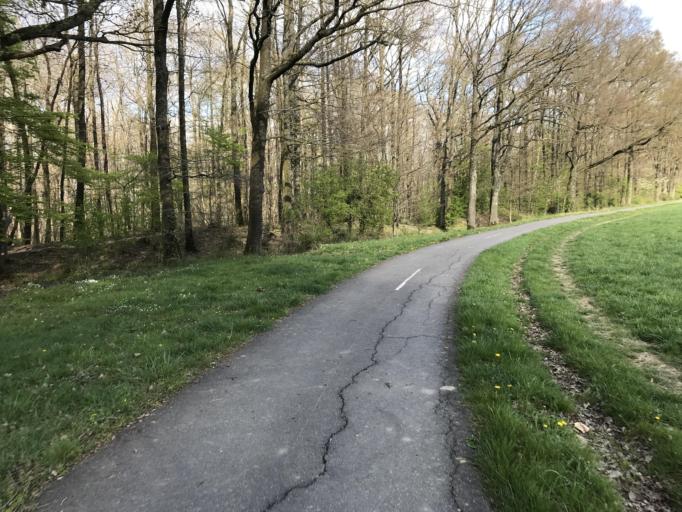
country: FR
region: Ile-de-France
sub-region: Departement de l'Essonne
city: Vauhallan
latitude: 48.7482
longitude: 2.2018
